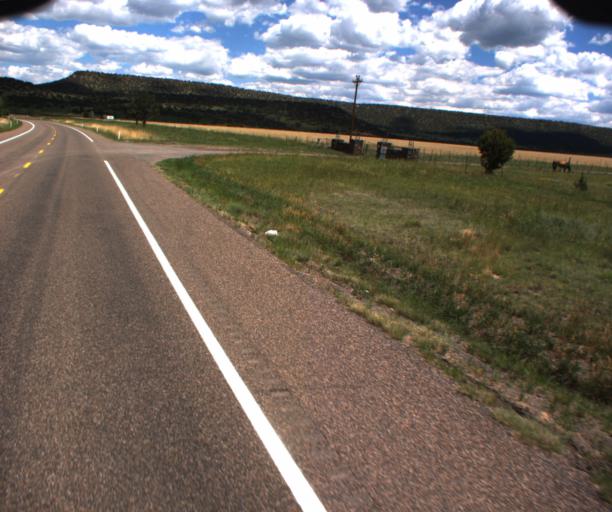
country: US
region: Arizona
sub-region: Apache County
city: Springerville
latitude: 34.1324
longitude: -109.2446
